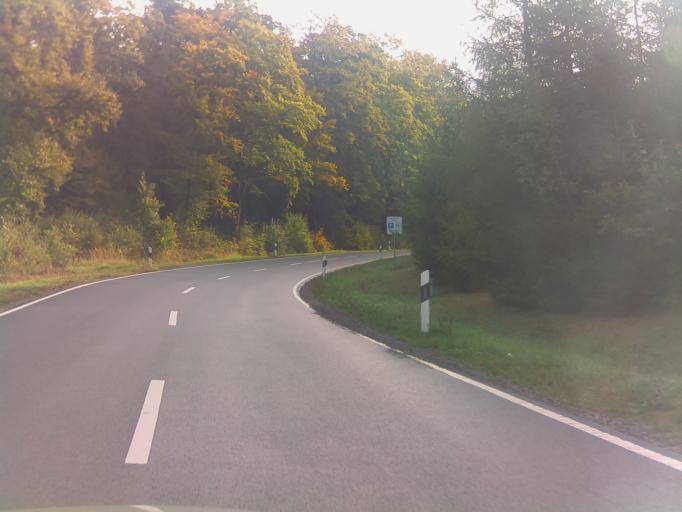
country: DE
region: Hesse
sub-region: Regierungsbezirk Kassel
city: Hosenfeld
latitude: 50.5048
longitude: 9.5416
